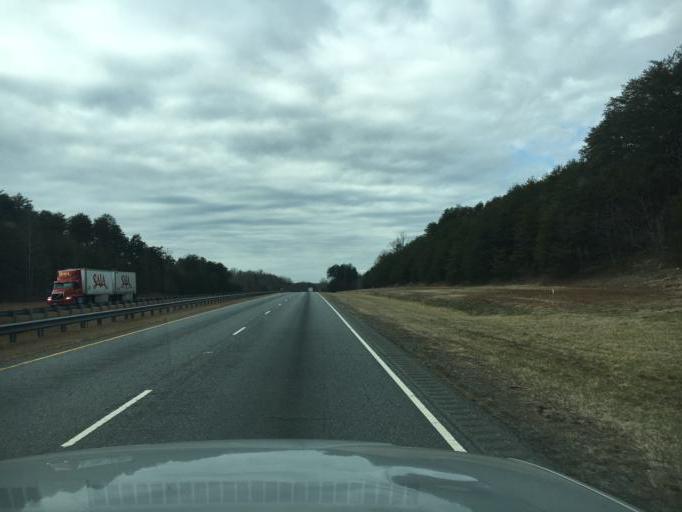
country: US
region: North Carolina
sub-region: Rutherford County
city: Spindale
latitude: 35.3020
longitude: -81.9638
